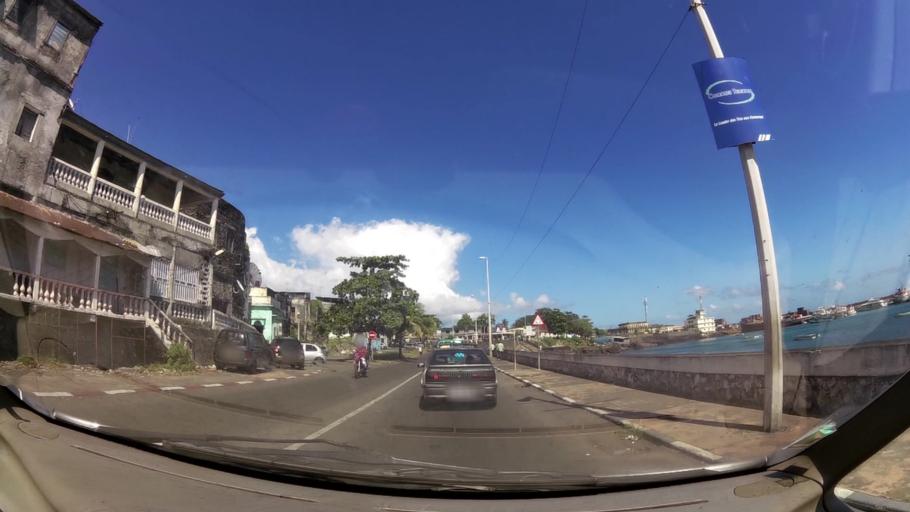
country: KM
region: Grande Comore
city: Moroni
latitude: -11.7038
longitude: 43.2512
